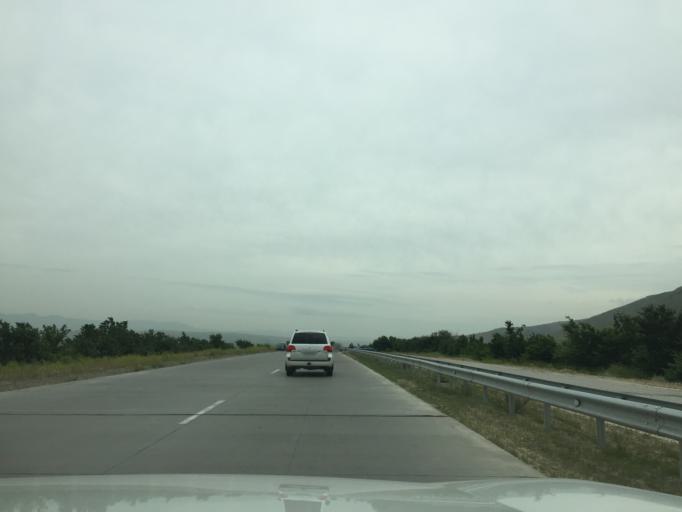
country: KZ
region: Ongtustik Qazaqstan
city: Sastobe
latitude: 42.5428
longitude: 70.0557
